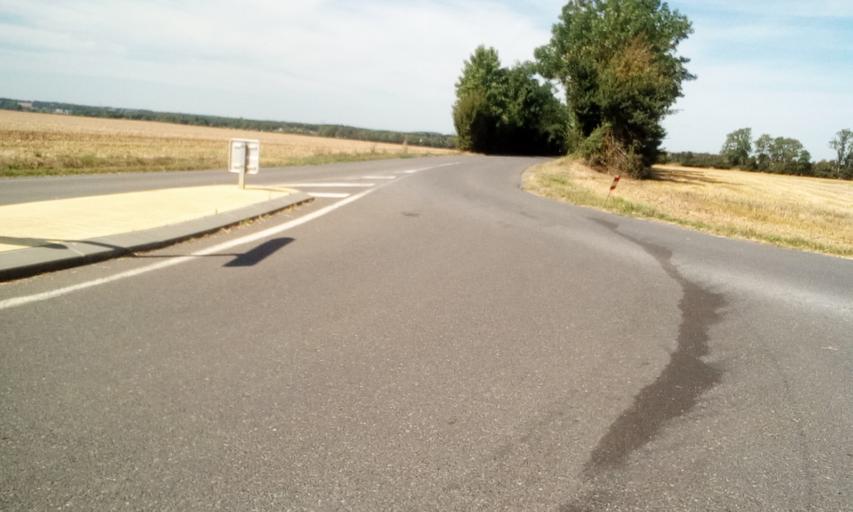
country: FR
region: Lower Normandy
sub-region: Departement du Calvados
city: Fontaine-Etoupefour
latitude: 49.1243
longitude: -0.4612
